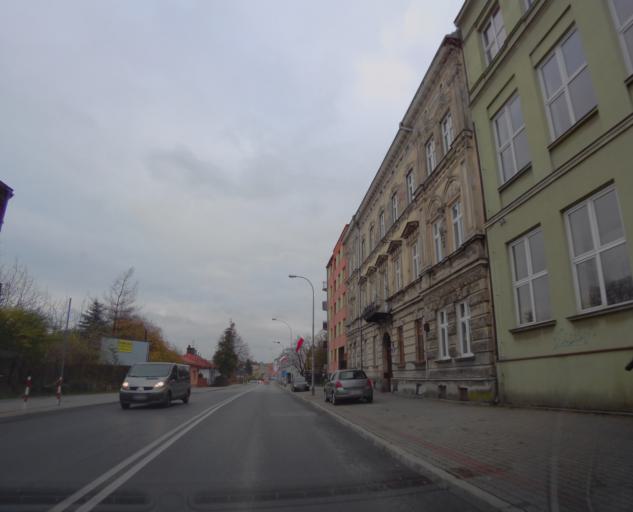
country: PL
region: Subcarpathian Voivodeship
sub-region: Powiat jaroslawski
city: Jaroslaw
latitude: 50.0166
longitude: 22.6855
